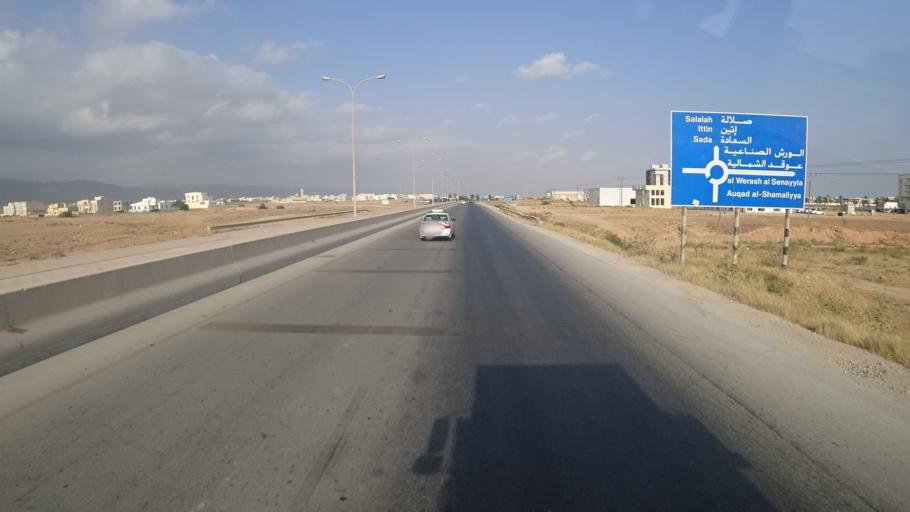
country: OM
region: Zufar
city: Salalah
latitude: 17.0288
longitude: 54.0259
